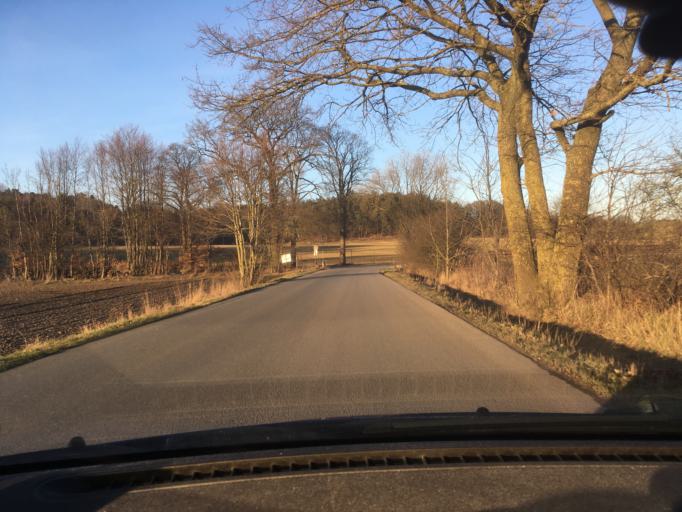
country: DE
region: Lower Saxony
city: Seevetal
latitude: 53.3861
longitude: 9.9557
